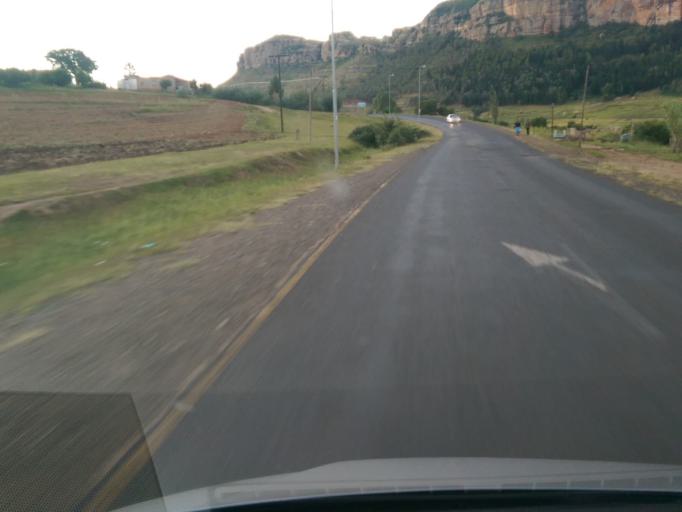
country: LS
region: Maseru
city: Nako
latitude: -29.4384
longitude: 27.7025
